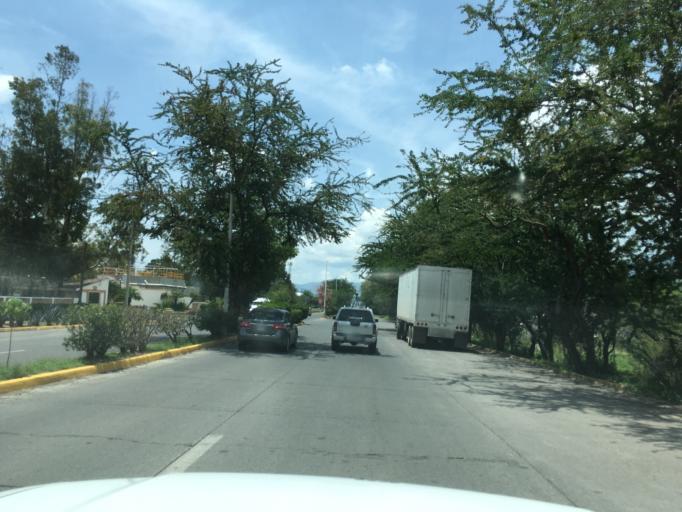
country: MX
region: Jalisco
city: Tlajomulco de Zuniga
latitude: 20.4640
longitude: -103.4473
